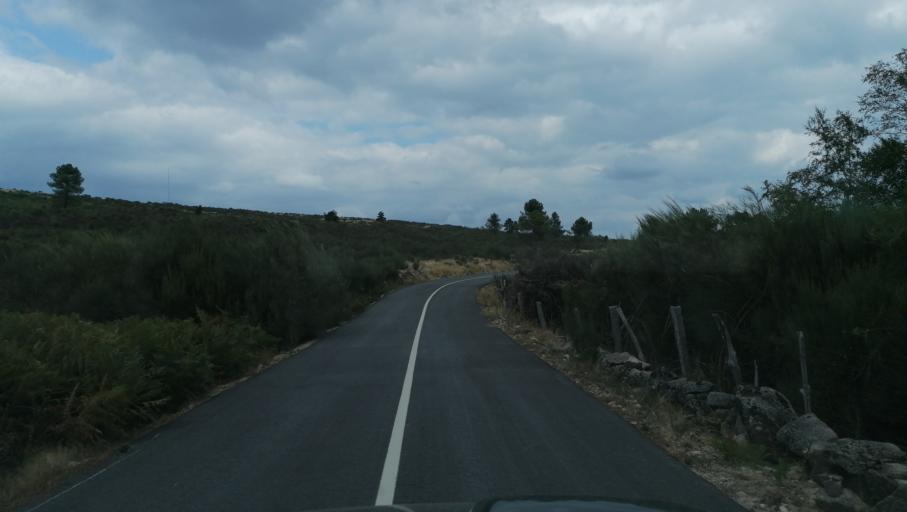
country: PT
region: Vila Real
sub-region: Vila Pouca de Aguiar
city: Vila Pouca de Aguiar
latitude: 41.5440
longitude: -7.6754
